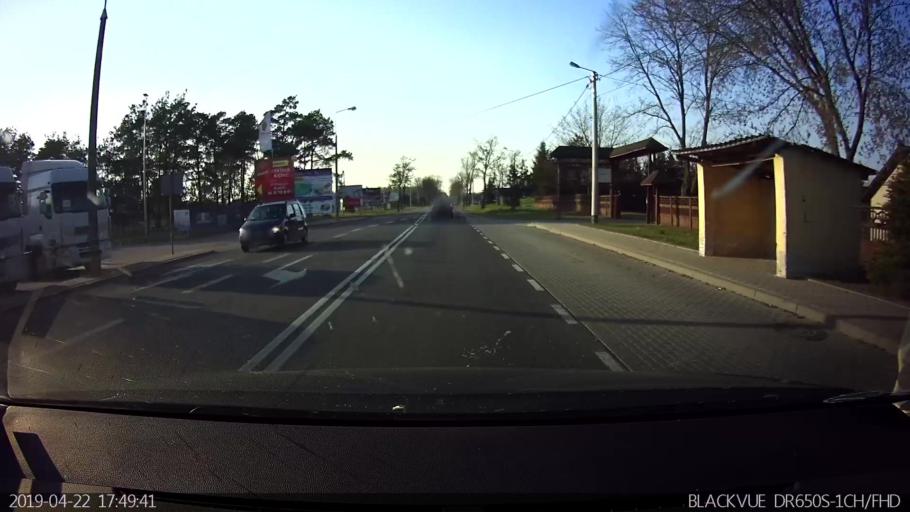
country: PL
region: Masovian Voivodeship
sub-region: Powiat wegrowski
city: Wegrow
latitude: 52.4162
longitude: 22.0073
